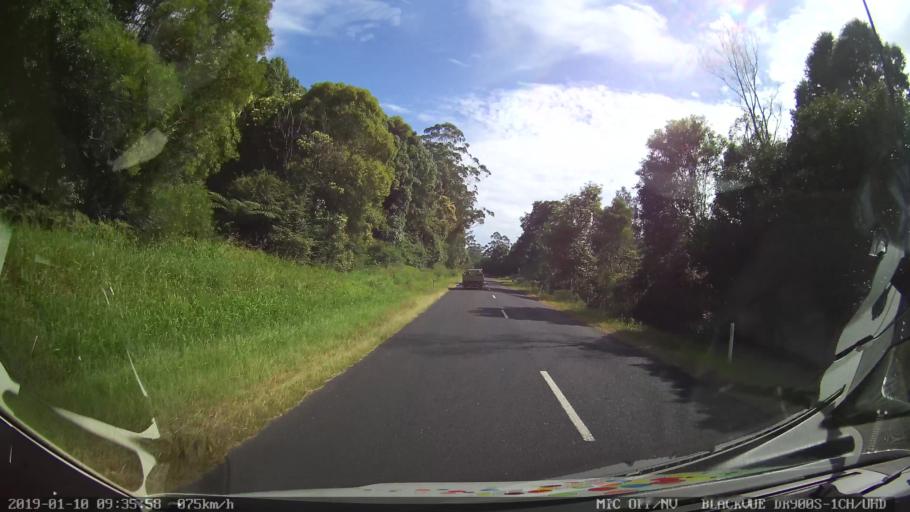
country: AU
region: New South Wales
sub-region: Coffs Harbour
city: Nana Glen
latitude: -30.2041
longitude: 153.0131
